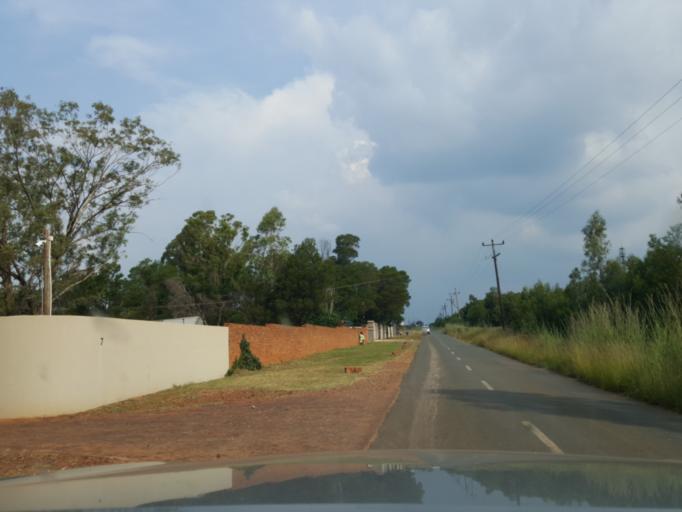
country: ZA
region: Gauteng
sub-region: City of Tshwane Metropolitan Municipality
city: Centurion
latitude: -25.8644
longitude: 28.3292
